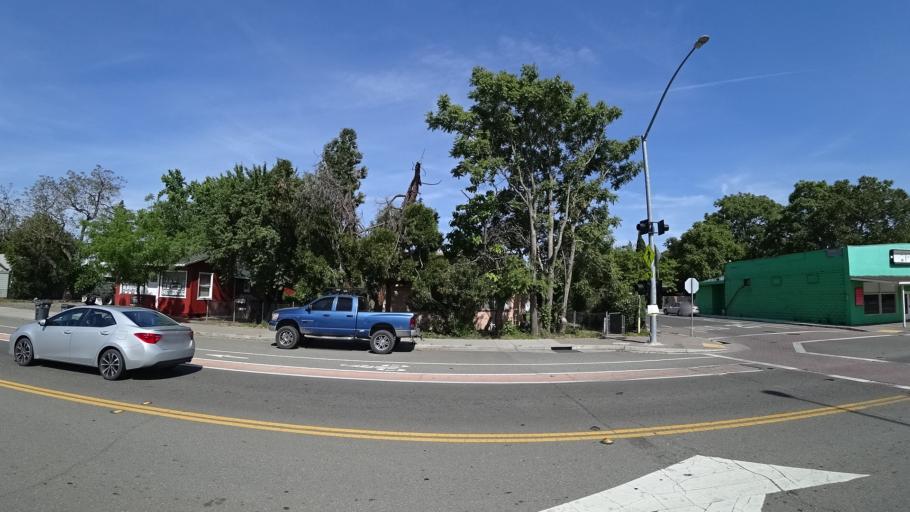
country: US
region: California
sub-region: Tehama County
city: Los Molinos
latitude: 40.0252
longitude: -122.0999
